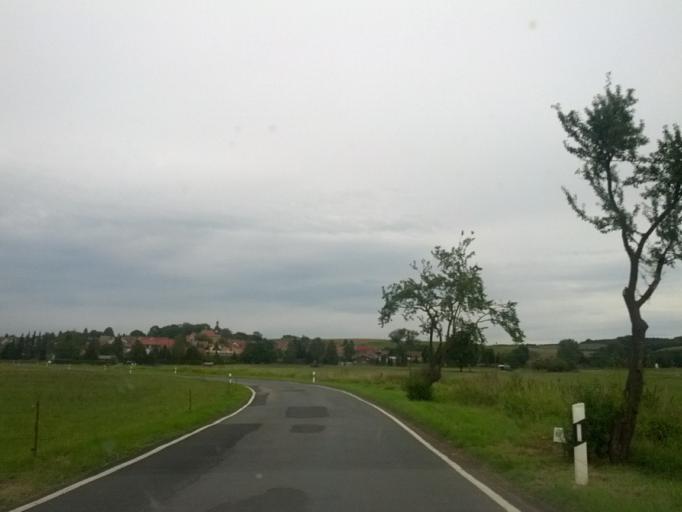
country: DE
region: Thuringia
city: Bad Salzungen
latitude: 50.8556
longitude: 10.2531
